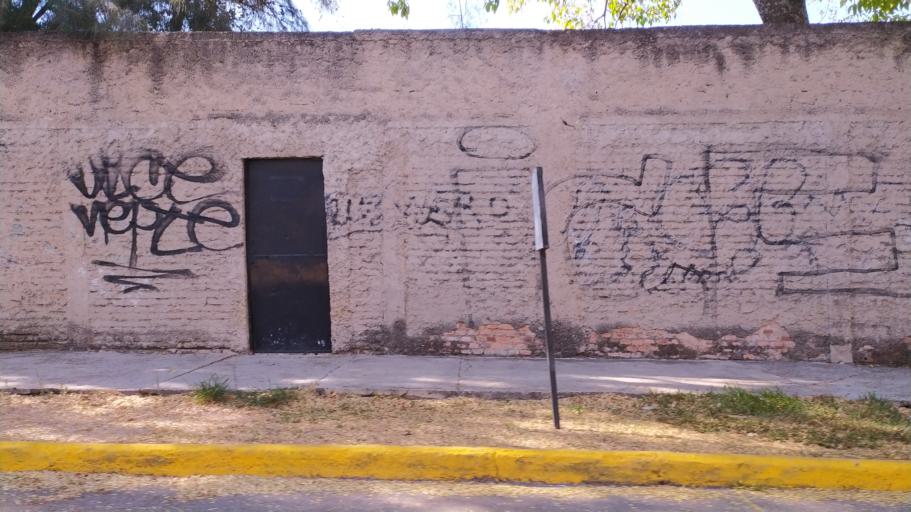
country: MX
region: Jalisco
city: Guadalajara
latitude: 20.6894
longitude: -103.3796
